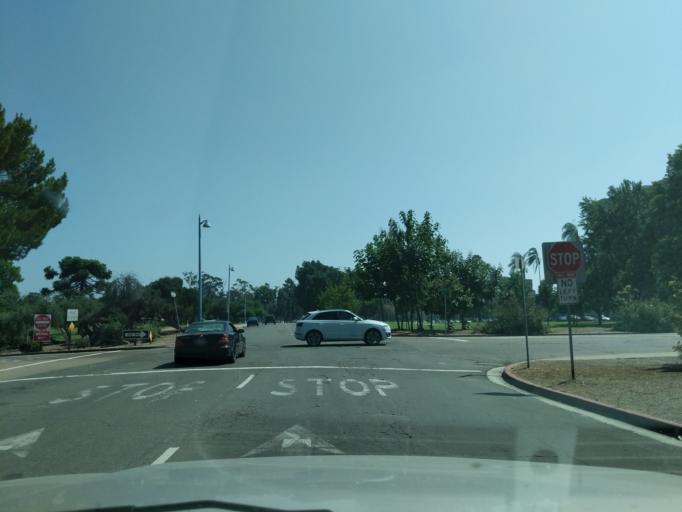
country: US
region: California
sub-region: San Diego County
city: San Diego
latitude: 32.7369
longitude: -117.1585
